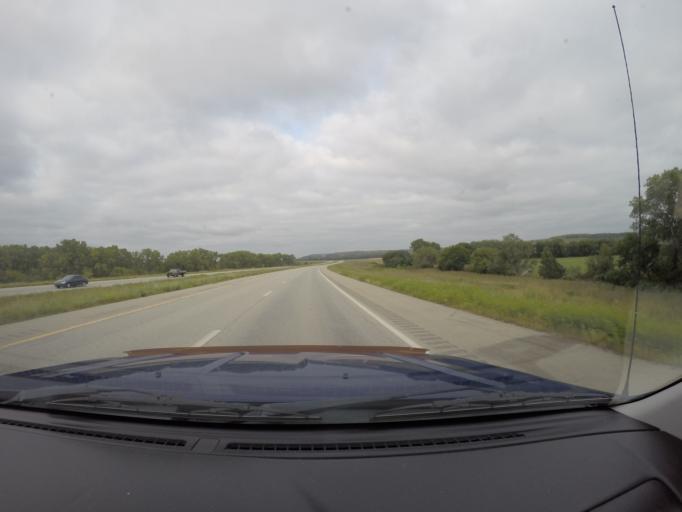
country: US
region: Kansas
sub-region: Riley County
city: Ogden
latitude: 39.0820
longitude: -96.7286
